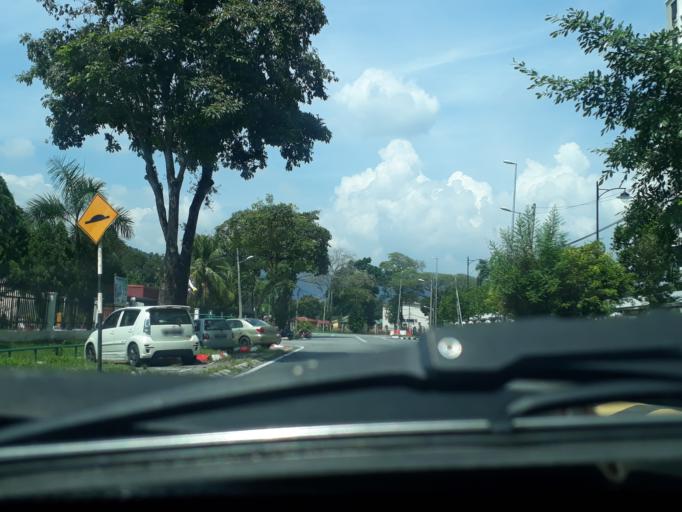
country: MY
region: Perak
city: Ipoh
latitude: 4.5945
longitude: 101.1153
